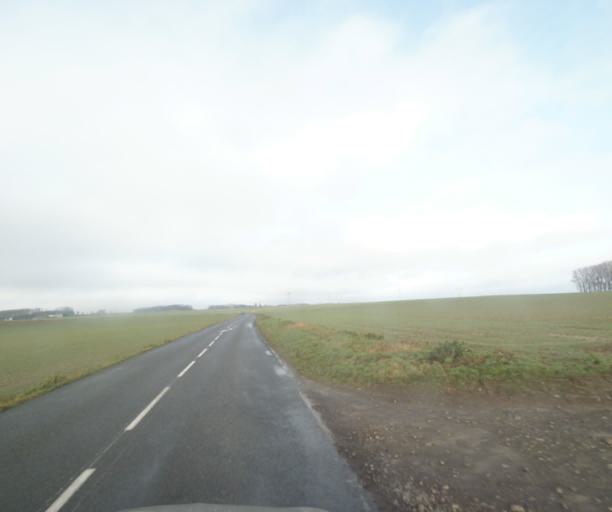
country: FR
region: Nord-Pas-de-Calais
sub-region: Departement du Nord
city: Artres
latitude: 50.2965
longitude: 3.5300
